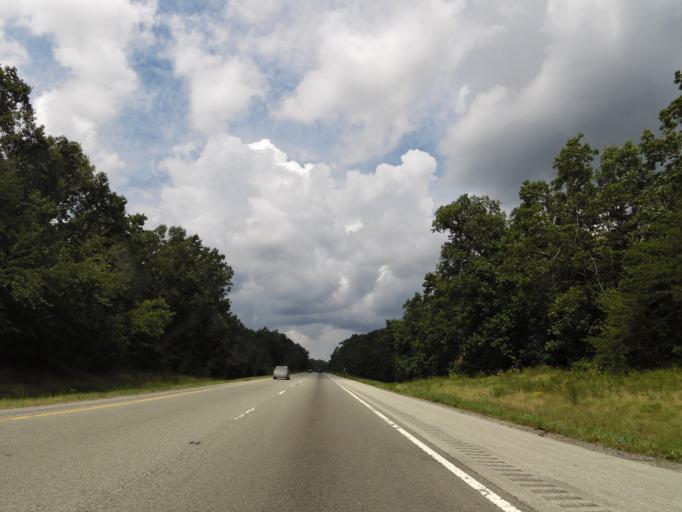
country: US
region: Tennessee
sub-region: Putnam County
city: Monterey
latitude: 36.0847
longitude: -85.2172
